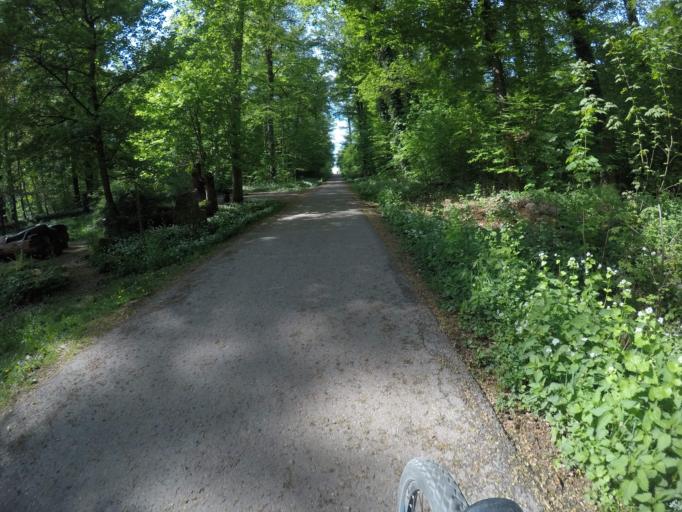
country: DE
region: Baden-Wuerttemberg
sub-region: Tuebingen Region
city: Tuebingen
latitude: 48.5496
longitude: 9.0343
